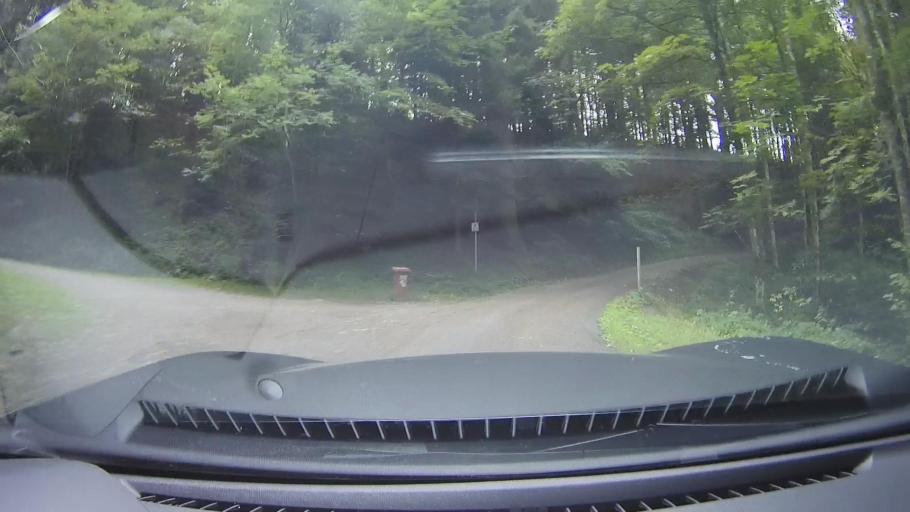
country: DE
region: Baden-Wuerttemberg
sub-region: Regierungsbezirk Stuttgart
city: Kaisersbach
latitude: 48.9531
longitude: 9.6463
